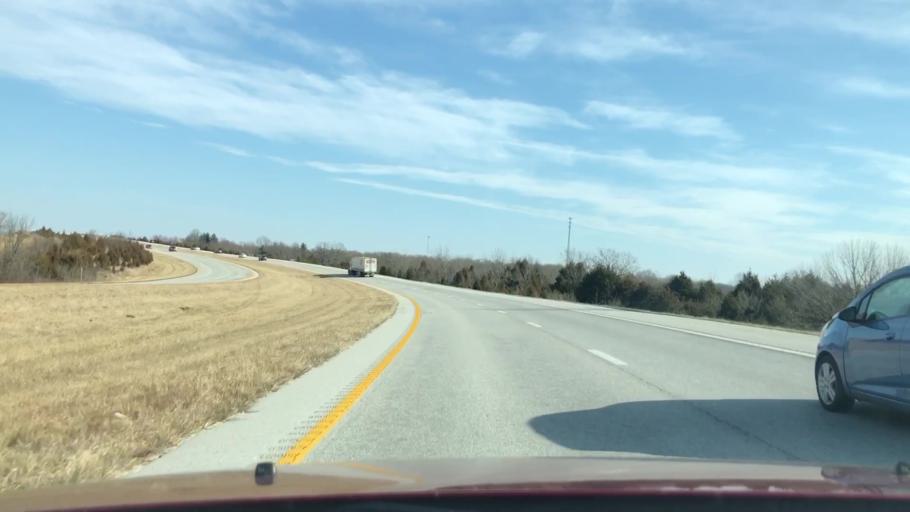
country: US
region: Missouri
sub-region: Webster County
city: Rogersville
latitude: 37.1527
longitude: -92.9384
